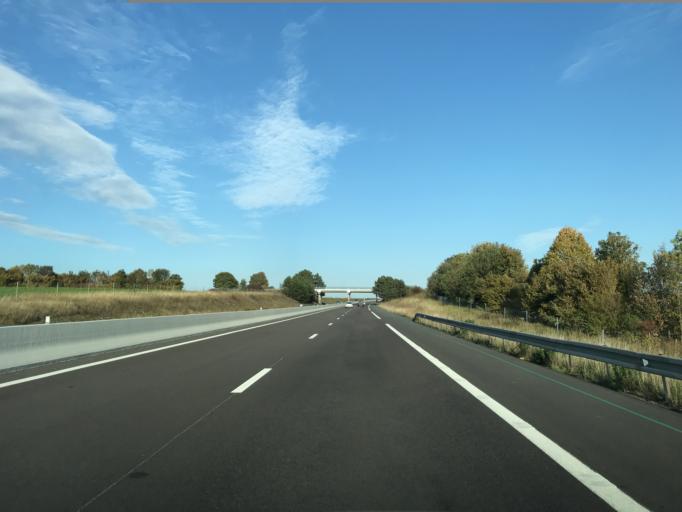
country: FR
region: Champagne-Ardenne
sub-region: Departement de la Marne
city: Sainte-Menehould
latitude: 49.0656
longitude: 4.7286
